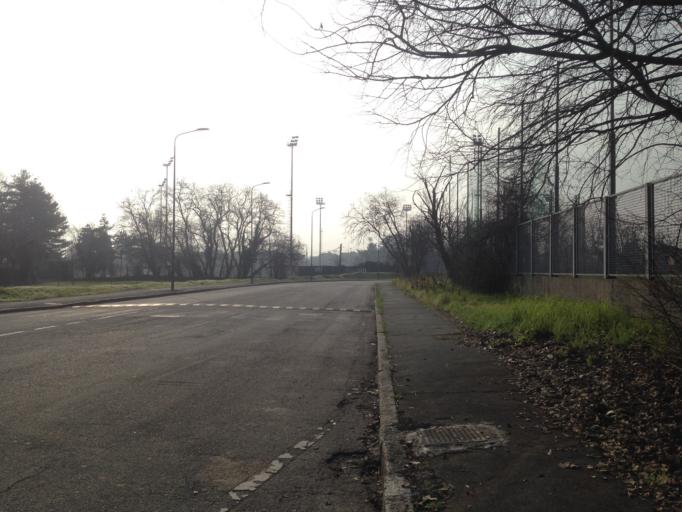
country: IT
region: Lombardy
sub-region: Citta metropolitana di Milano
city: Cesano Boscone
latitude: 45.4682
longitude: 9.1099
